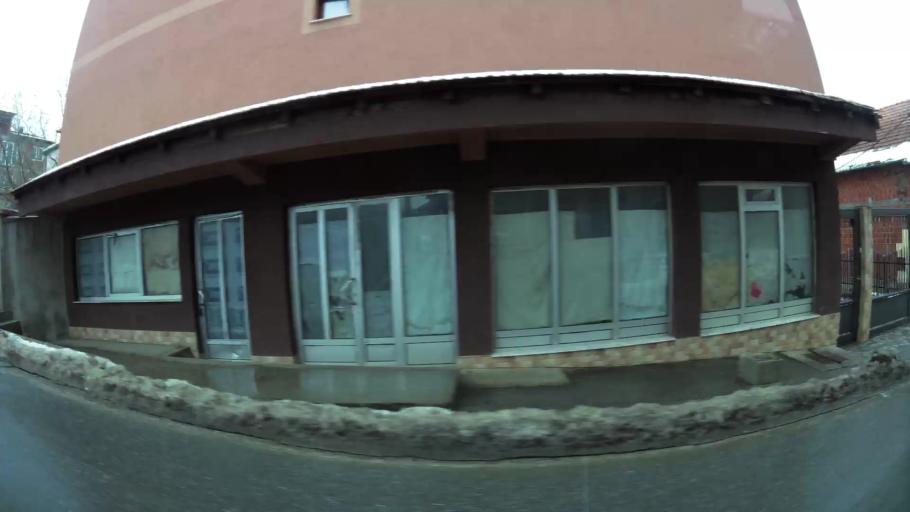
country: XK
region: Pristina
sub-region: Komuna e Prishtines
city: Pristina
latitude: 42.6622
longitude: 21.1811
